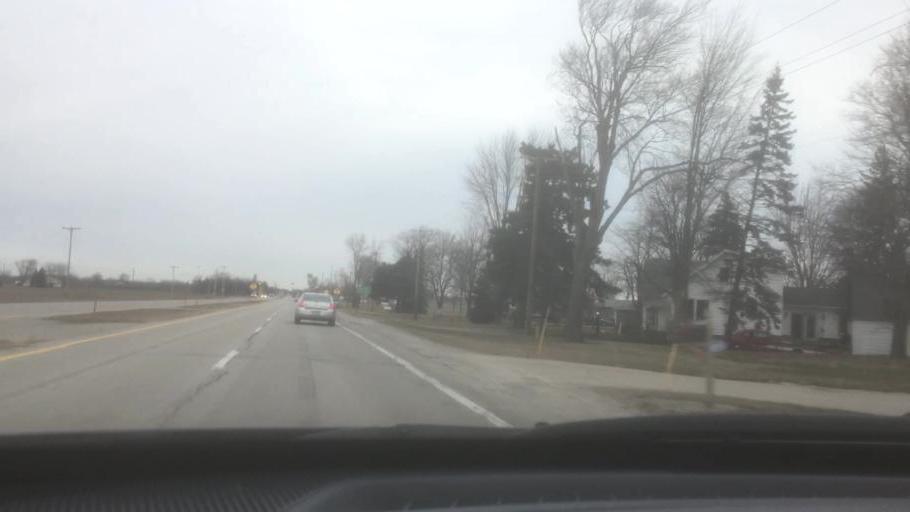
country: US
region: Michigan
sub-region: Bay County
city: Essexville
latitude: 43.5627
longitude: -83.8419
